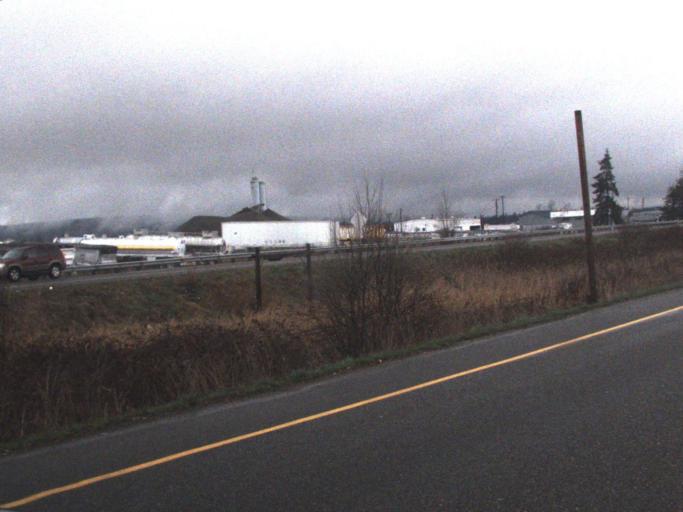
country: US
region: Washington
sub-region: Snohomish County
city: Marysville
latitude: 48.0258
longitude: -122.1847
